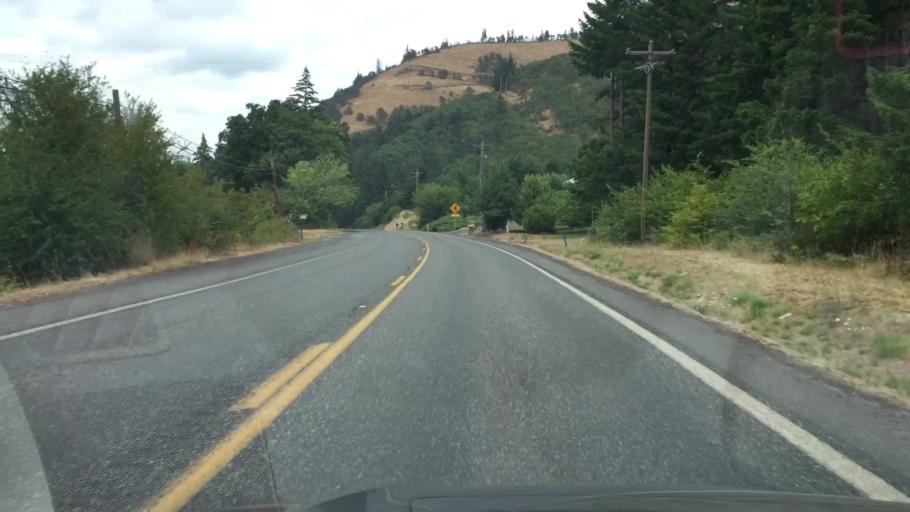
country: US
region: Washington
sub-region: Klickitat County
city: White Salmon
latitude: 45.7747
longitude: -121.5153
